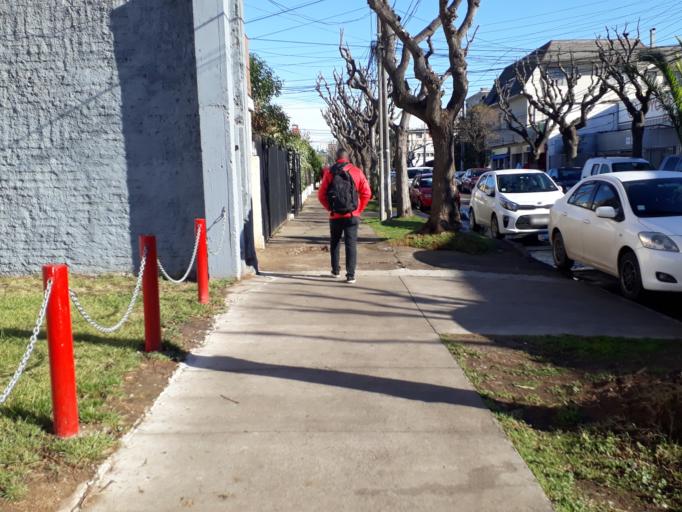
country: CL
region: Valparaiso
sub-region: Provincia de Valparaiso
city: Vina del Mar
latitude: -33.0142
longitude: -71.5437
